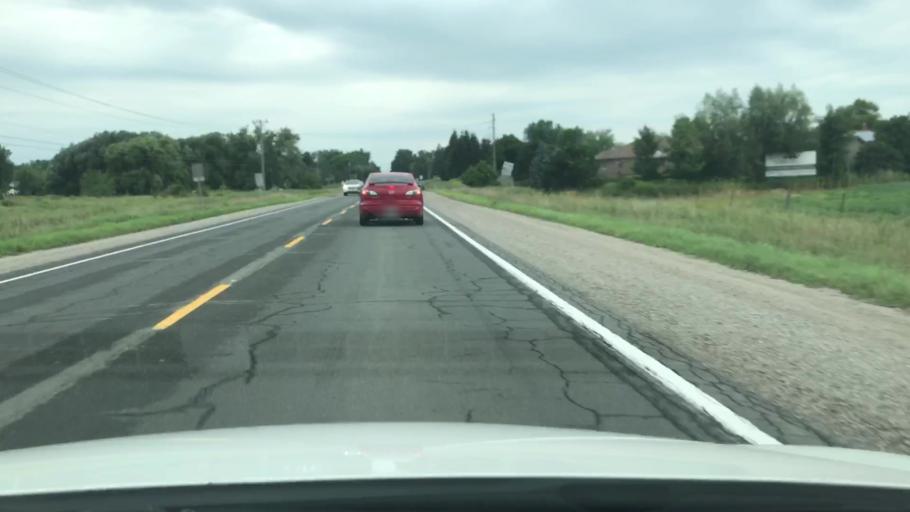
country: CA
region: Ontario
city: Innisfil
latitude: 44.3178
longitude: -79.6175
